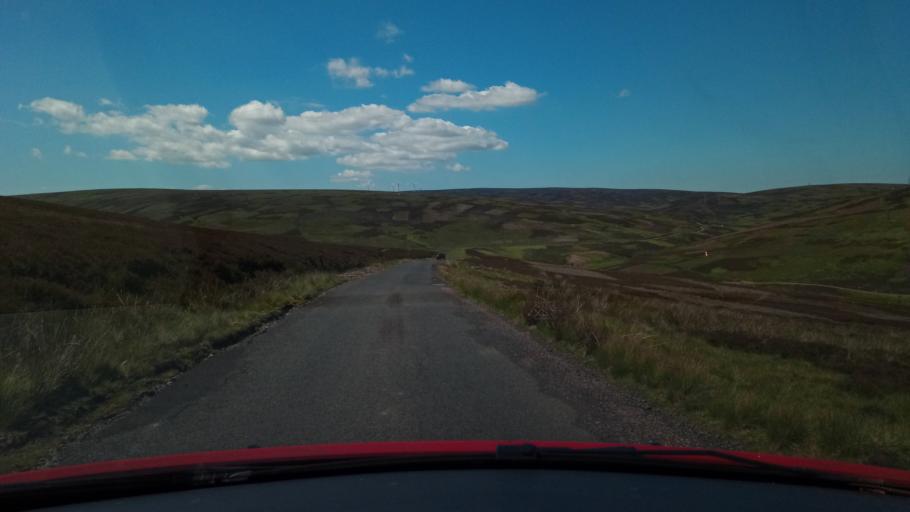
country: GB
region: Scotland
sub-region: East Lothian
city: Dunbar
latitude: 55.8451
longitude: -2.5700
